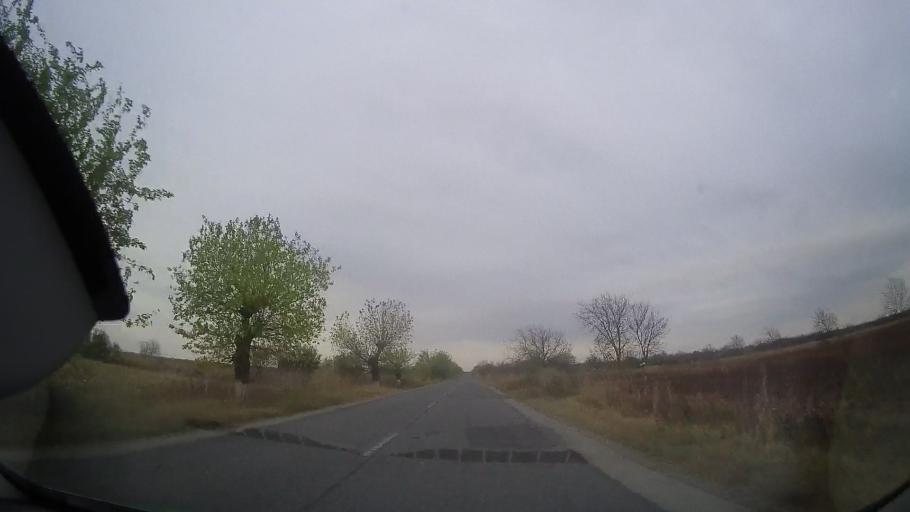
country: RO
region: Ialomita
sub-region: Comuna Milosesti
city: Milosesti
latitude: 44.7539
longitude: 27.2158
